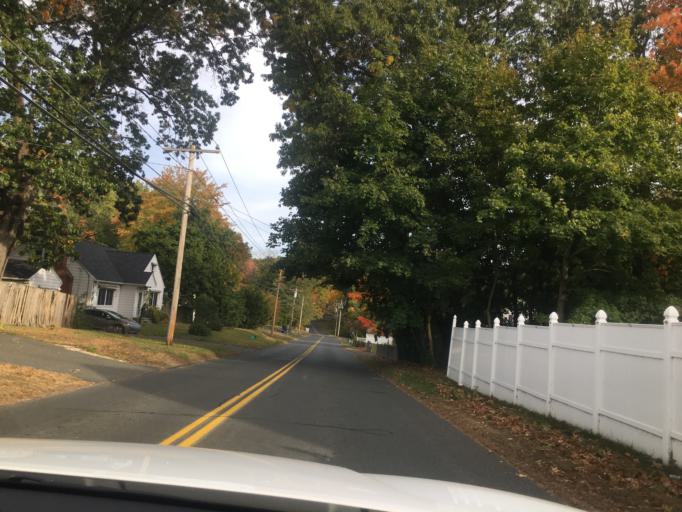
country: US
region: Connecticut
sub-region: Hartford County
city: Sherwood Manor
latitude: 42.0243
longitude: -72.5815
